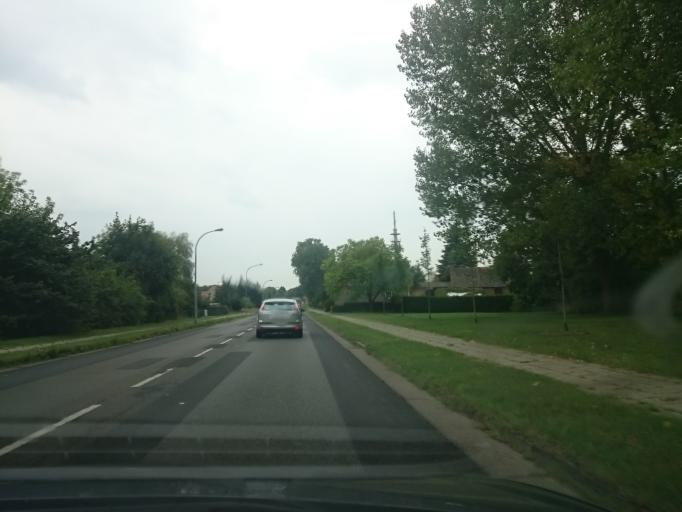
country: DE
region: Brandenburg
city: Gransee
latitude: 53.0021
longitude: 13.1589
